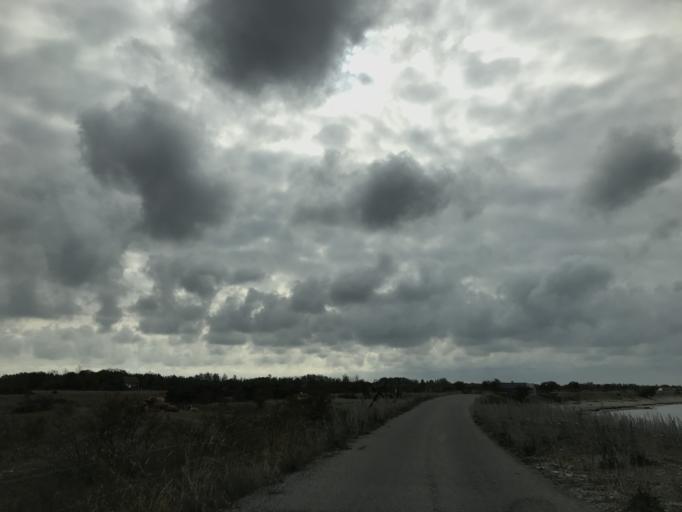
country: SE
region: Kalmar
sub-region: Borgholms Kommun
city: Borgholm
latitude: 57.0513
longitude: 16.8361
